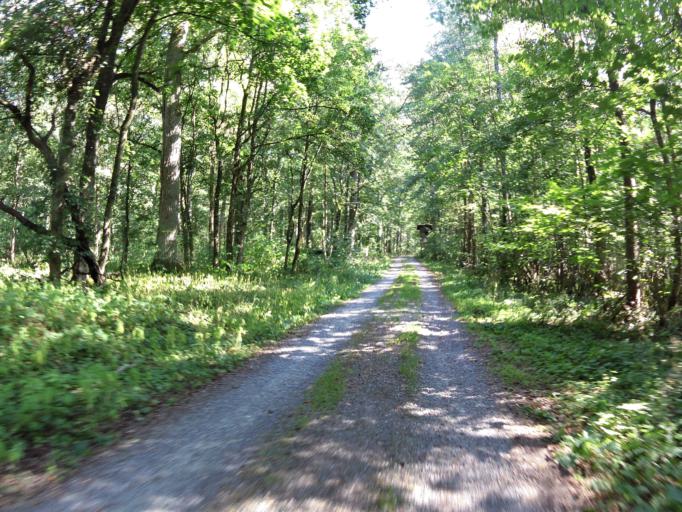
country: DE
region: Bavaria
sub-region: Regierungsbezirk Unterfranken
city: Margetshochheim
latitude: 49.8534
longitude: 9.8707
